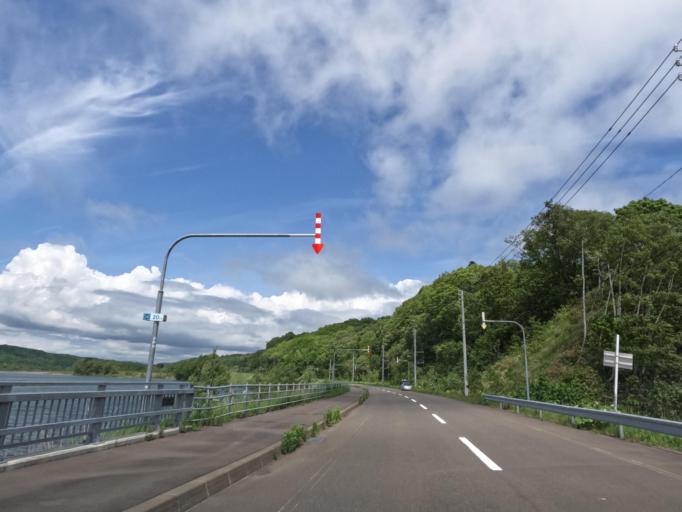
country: JP
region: Hokkaido
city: Tobetsu
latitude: 43.3623
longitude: 141.5701
